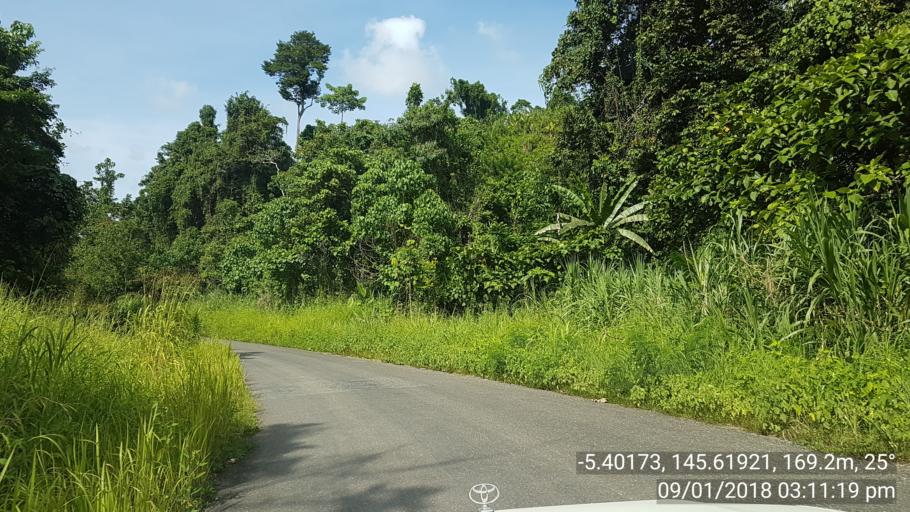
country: PG
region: Madang
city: Madang
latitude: -5.4019
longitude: 145.6192
